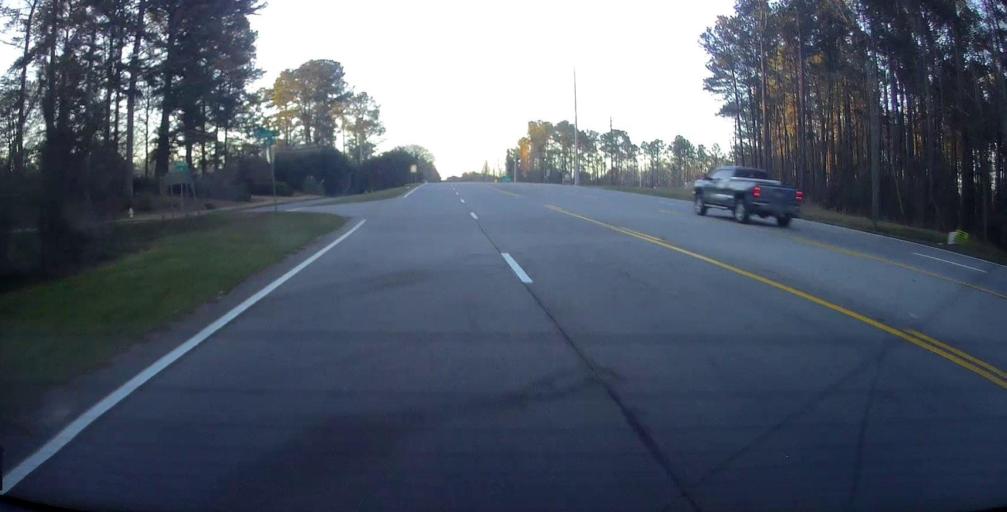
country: US
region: Alabama
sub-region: Russell County
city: Phenix City
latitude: 32.5251
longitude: -84.9910
